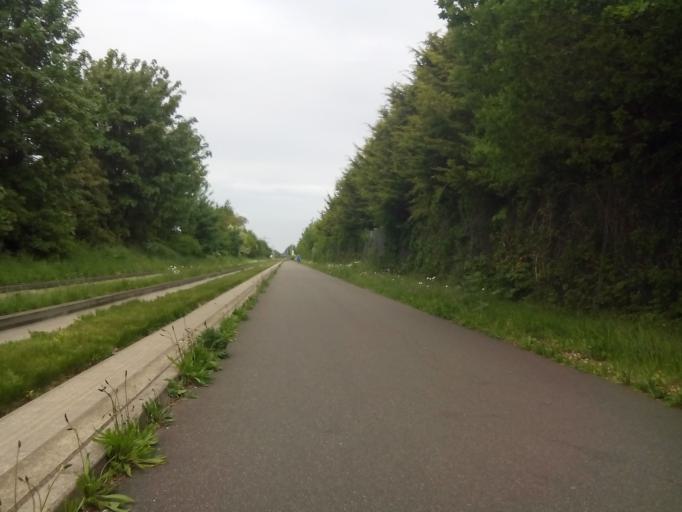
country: GB
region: England
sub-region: Cambridgeshire
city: Histon
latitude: 52.2319
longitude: 0.1413
